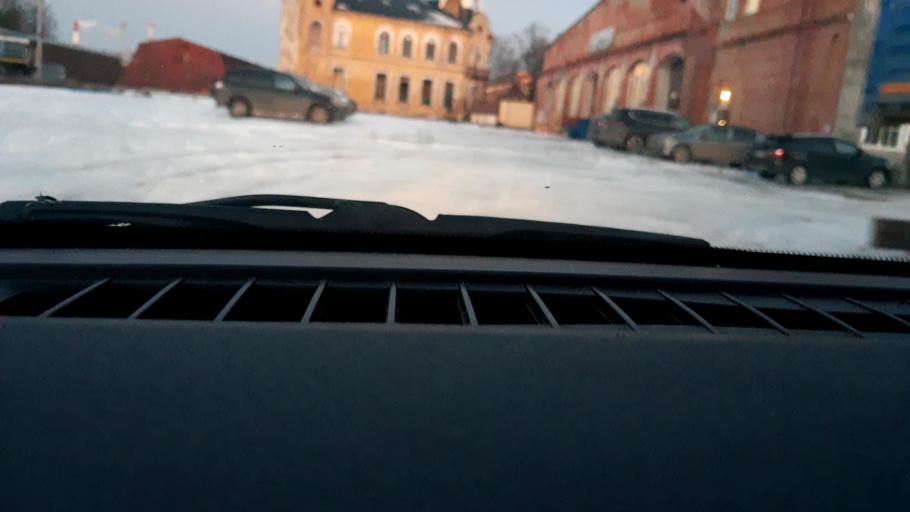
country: RU
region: Nizjnij Novgorod
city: Neklyudovo
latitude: 56.3546
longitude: 43.8727
